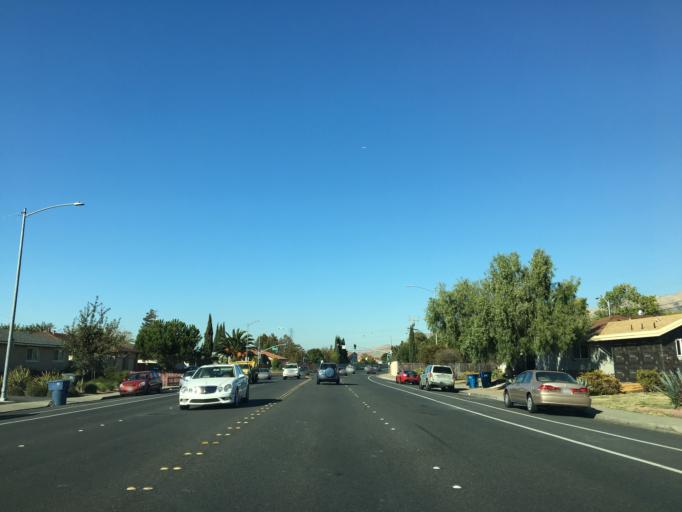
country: US
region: California
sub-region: Santa Clara County
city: Milpitas
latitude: 37.4384
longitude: -121.9113
